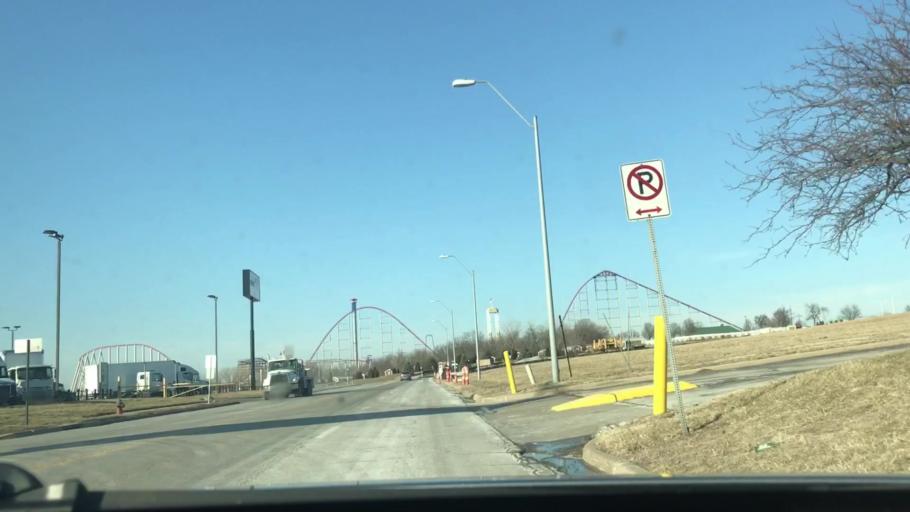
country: US
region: Missouri
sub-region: Clay County
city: Claycomo
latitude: 39.1666
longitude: -94.4886
